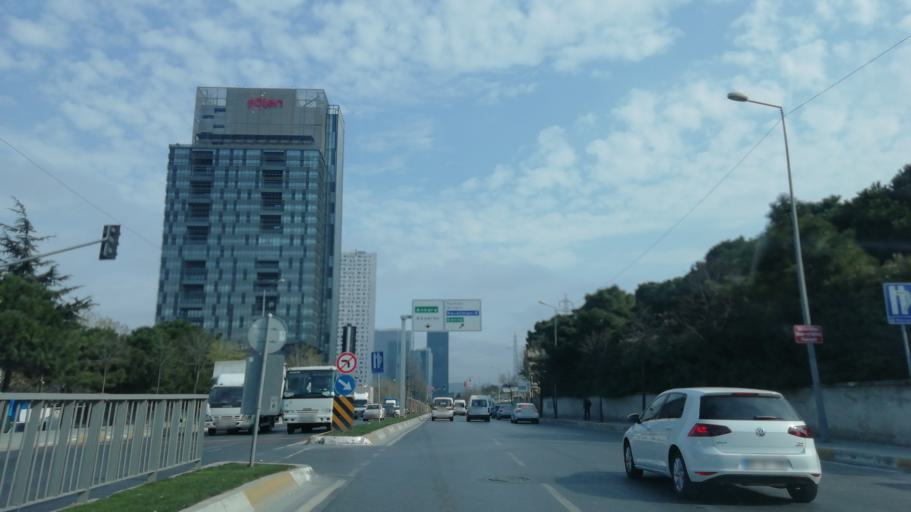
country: TR
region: Istanbul
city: Mahmutbey
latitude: 41.0502
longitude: 28.8124
